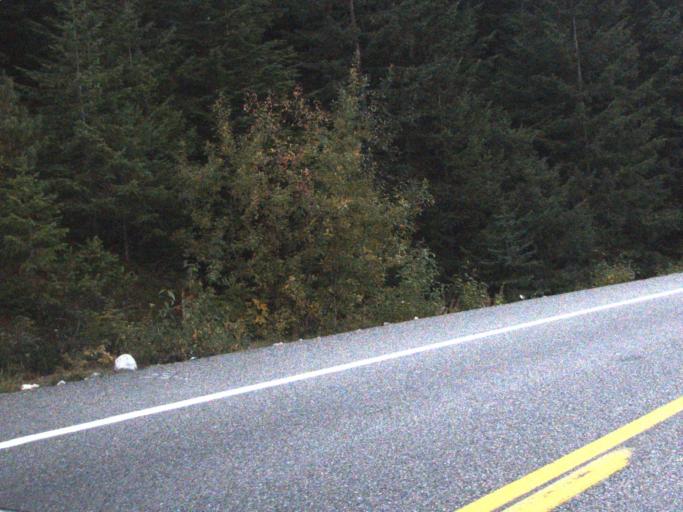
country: US
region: Washington
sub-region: Snohomish County
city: Darrington
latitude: 48.6622
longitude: -120.8674
